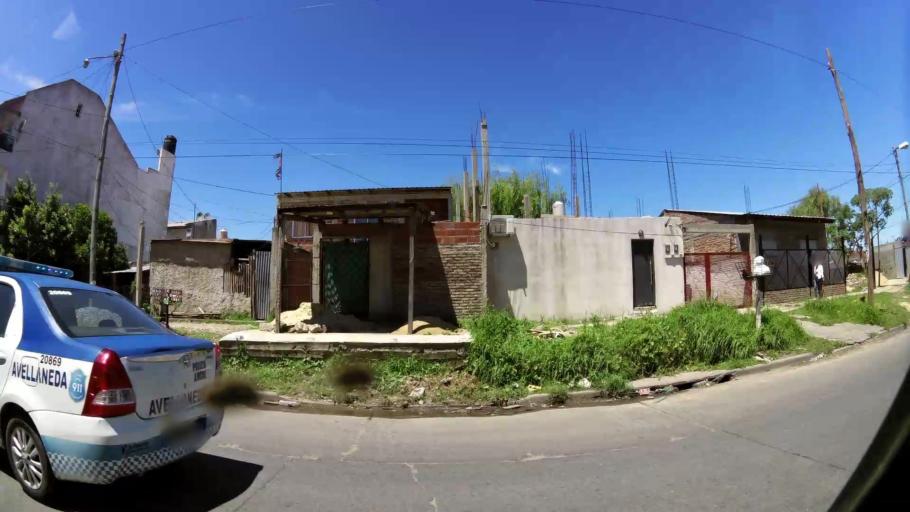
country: AR
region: Buenos Aires
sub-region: Partido de Quilmes
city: Quilmes
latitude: -34.7148
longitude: -58.3205
